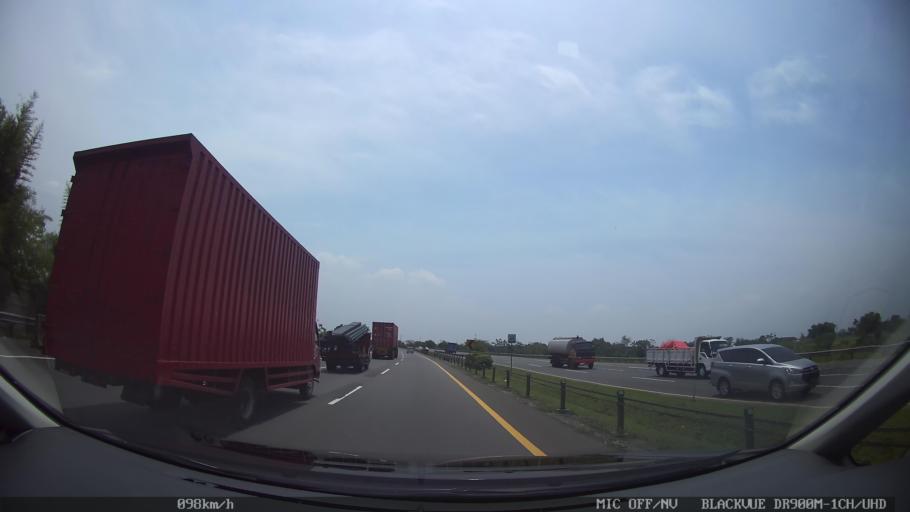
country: ID
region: West Java
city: Kresek
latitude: -6.1851
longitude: 106.4055
